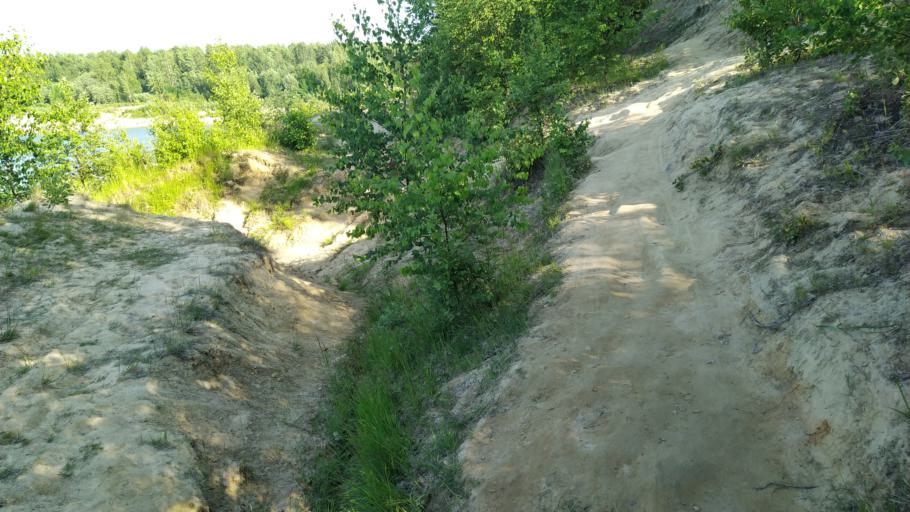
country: RU
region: Leningrad
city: Toksovo
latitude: 60.1146
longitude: 30.5377
